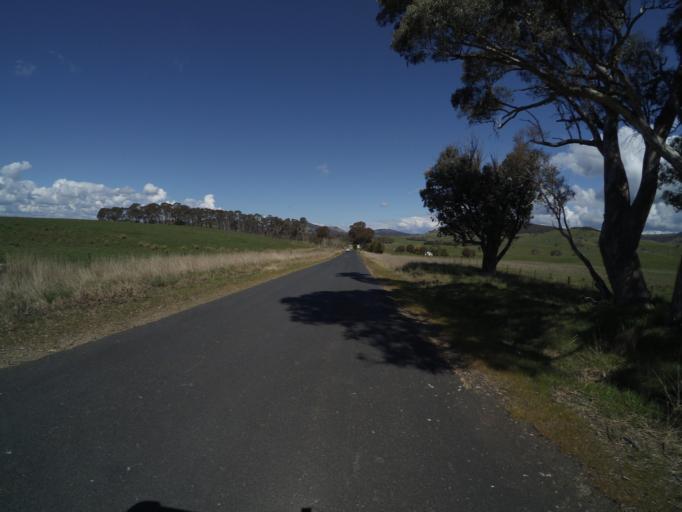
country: AU
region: New South Wales
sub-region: Yass Valley
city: Murrumbateman
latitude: -35.1252
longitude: 148.8691
